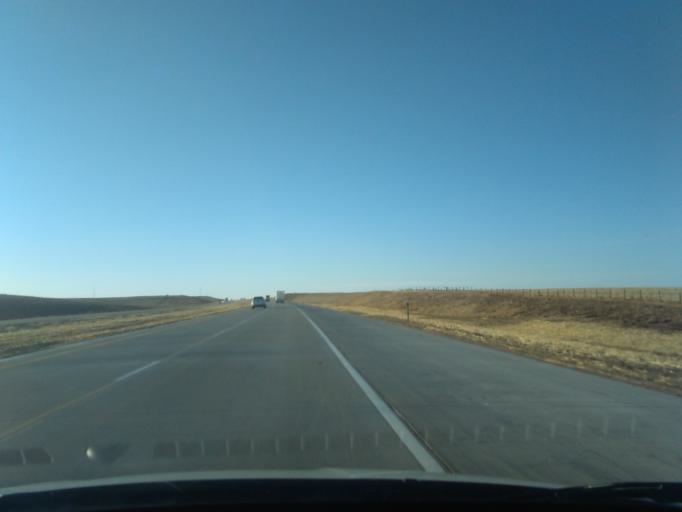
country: US
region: Nebraska
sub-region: Deuel County
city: Chappell
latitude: 41.1127
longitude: -102.5732
